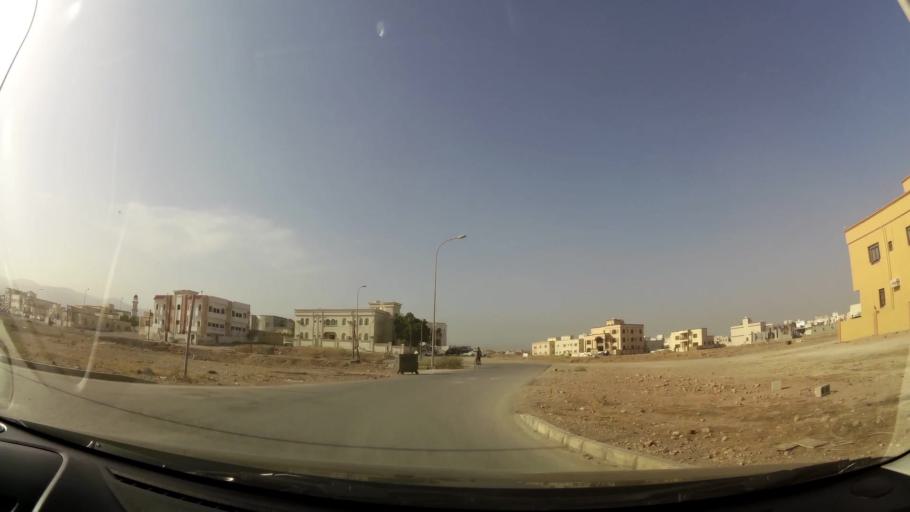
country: OM
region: Zufar
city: Salalah
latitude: 17.0119
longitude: 54.0192
